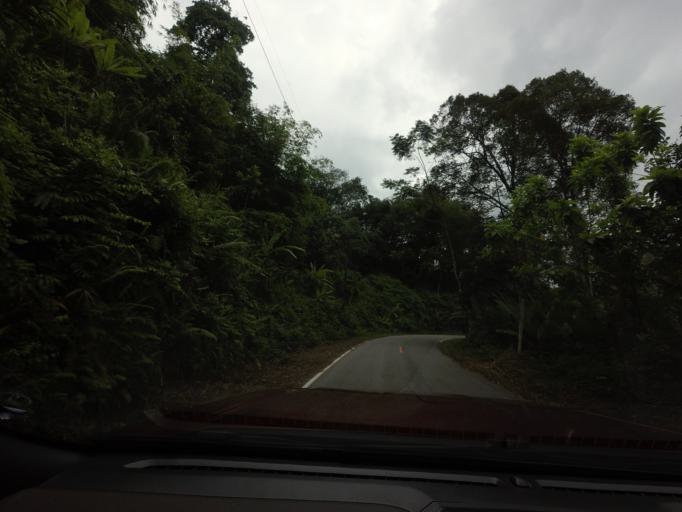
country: TH
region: Narathiwat
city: Sukhirin
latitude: 5.9760
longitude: 101.6806
